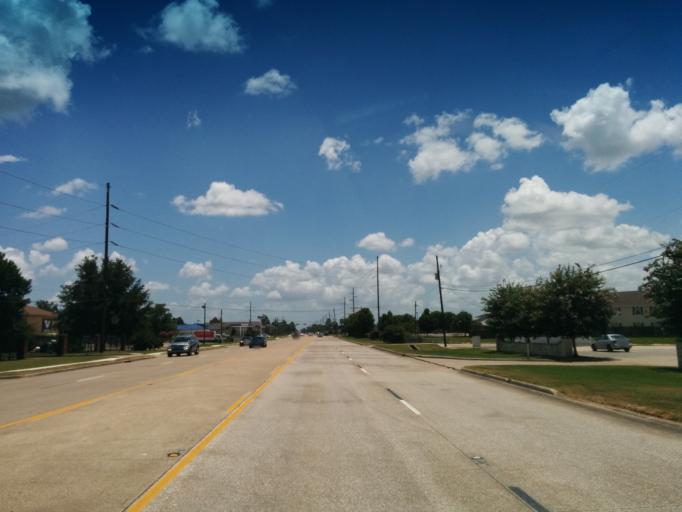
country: US
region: Texas
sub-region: Jefferson County
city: Beaumont
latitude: 30.0940
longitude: -94.1900
